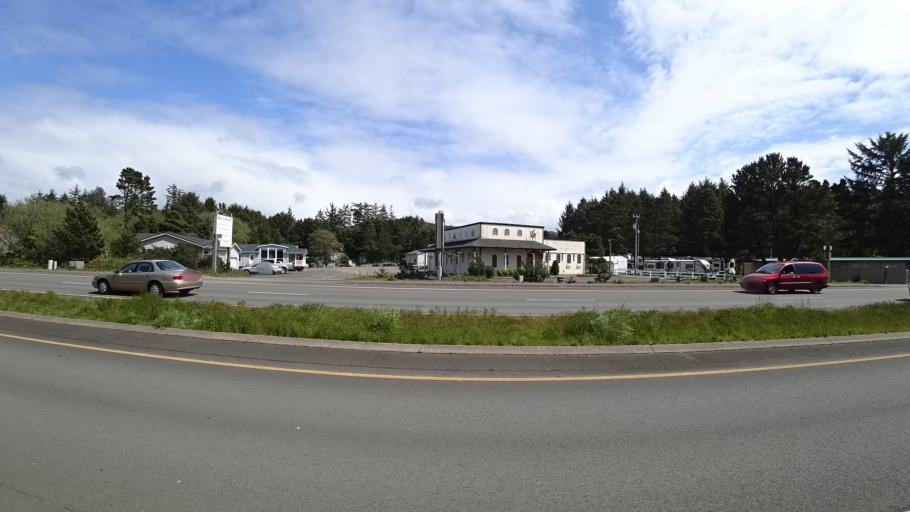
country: US
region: Oregon
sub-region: Lincoln County
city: Lincoln Beach
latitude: 44.8444
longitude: -124.0474
